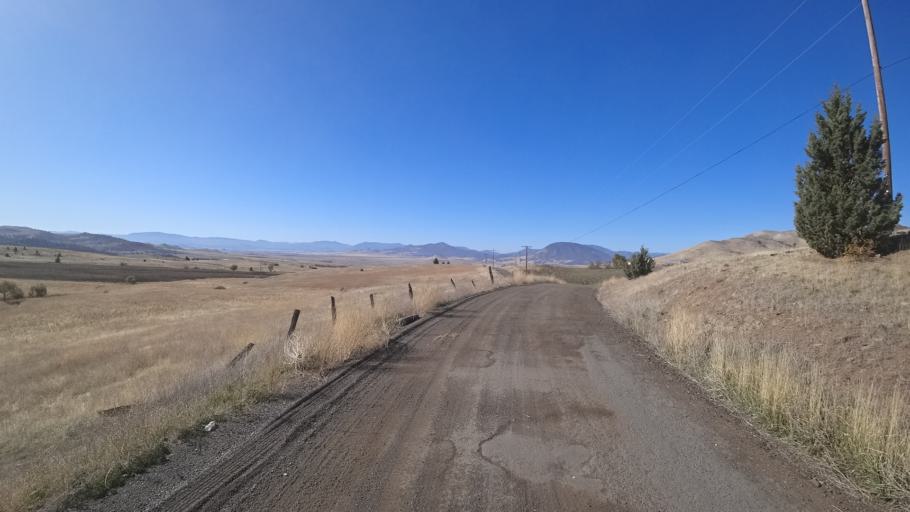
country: US
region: California
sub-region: Siskiyou County
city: Montague
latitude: 41.8299
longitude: -122.3567
